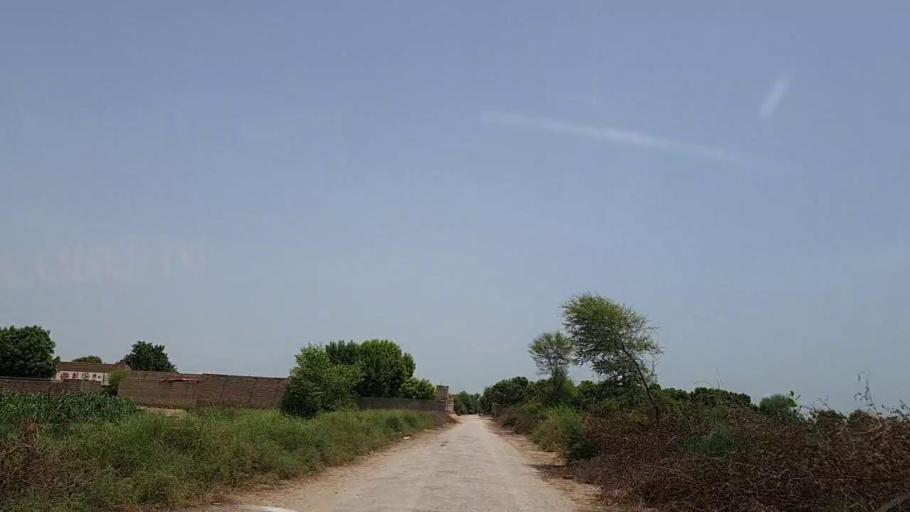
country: PK
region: Sindh
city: Tharu Shah
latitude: 26.9556
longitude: 68.0276
